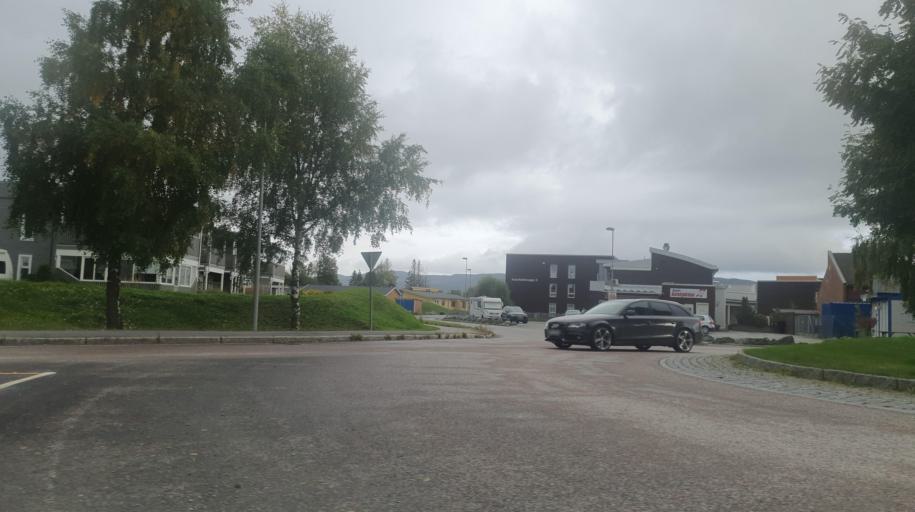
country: NO
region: Nord-Trondelag
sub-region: Verdal
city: Verdal
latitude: 63.7926
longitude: 11.4902
